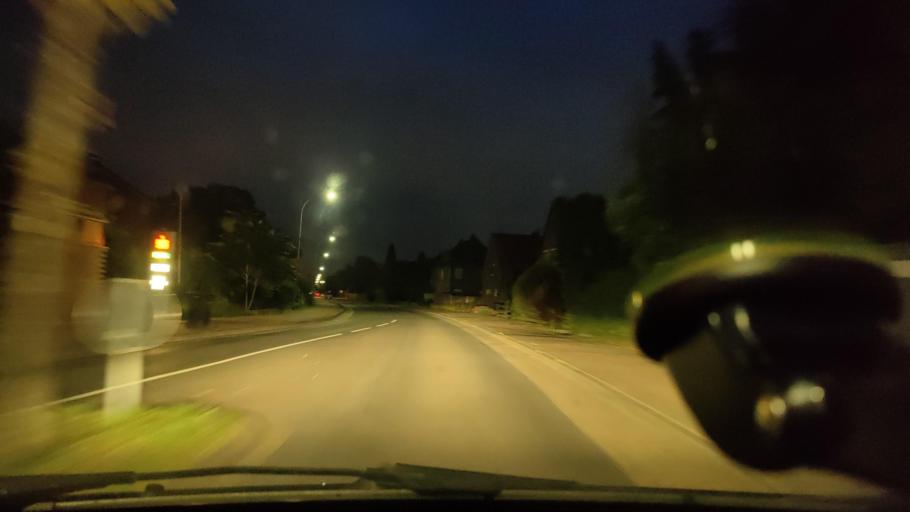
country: DE
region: North Rhine-Westphalia
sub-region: Regierungsbezirk Dusseldorf
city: Alpen
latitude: 51.5906
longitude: 6.5602
